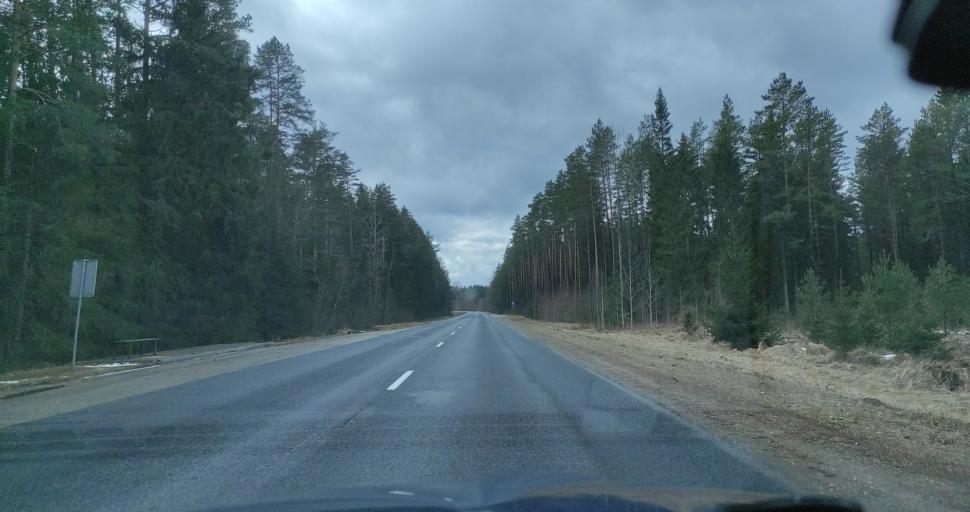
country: LV
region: Talsu Rajons
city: Stende
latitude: 57.1081
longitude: 22.4951
